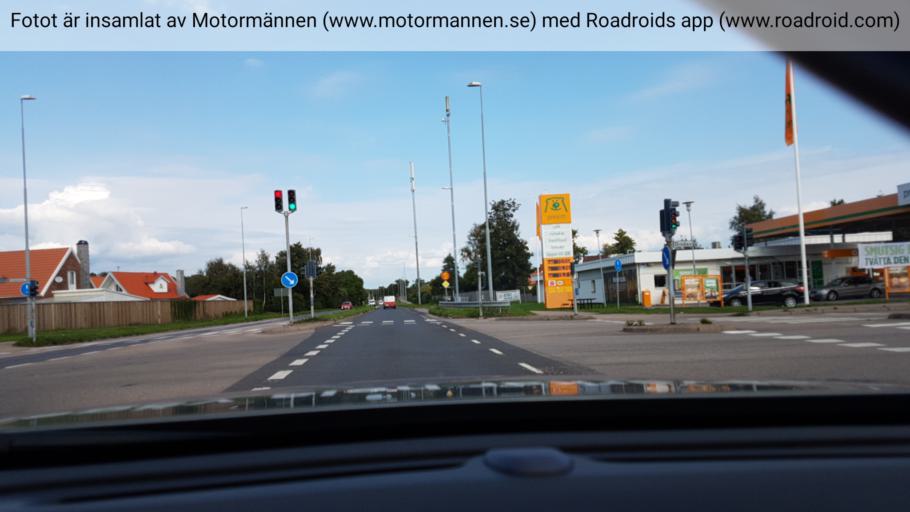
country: SE
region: Halland
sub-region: Halmstads Kommun
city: Mjallby
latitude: 56.6598
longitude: 12.8067
